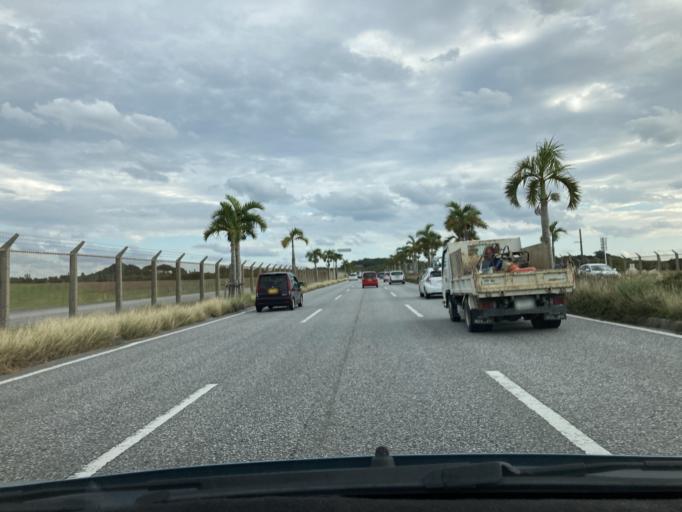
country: JP
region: Okinawa
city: Chatan
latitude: 26.3428
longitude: 127.7490
